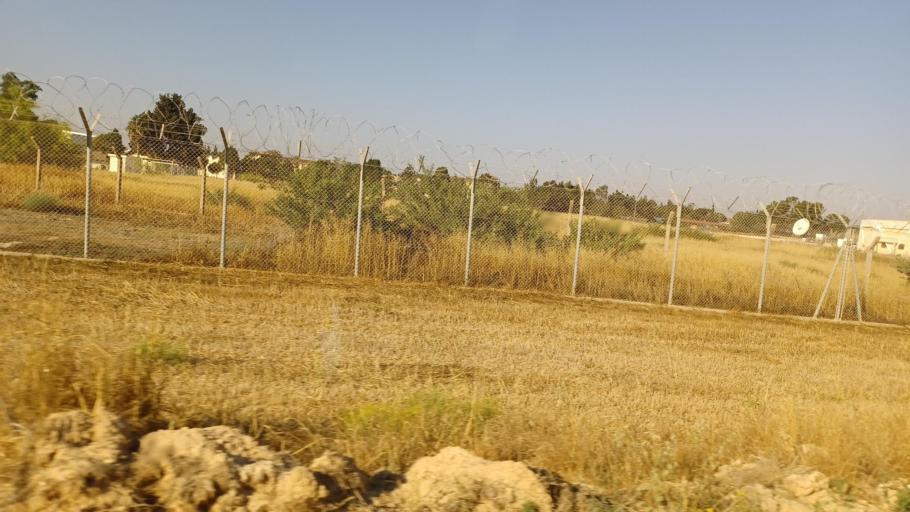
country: CY
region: Ammochostos
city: Acheritou
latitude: 35.0942
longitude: 33.8902
